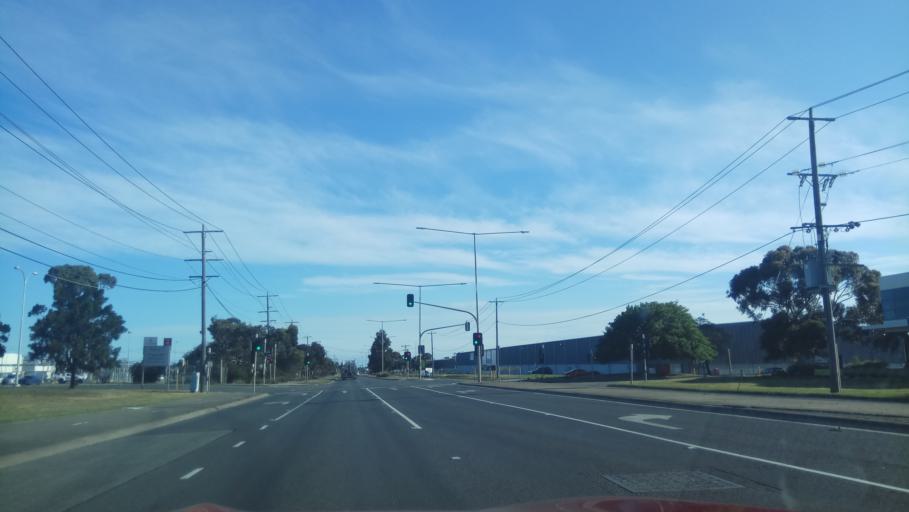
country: AU
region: Victoria
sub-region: Hobsons Bay
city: Altona North
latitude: -37.8335
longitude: 144.8265
